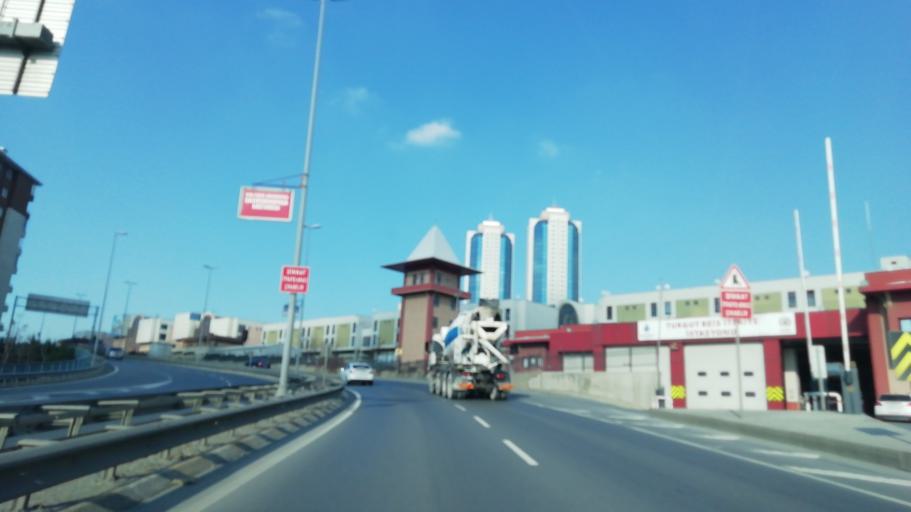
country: TR
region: Istanbul
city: Esenler
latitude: 41.0642
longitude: 28.8672
